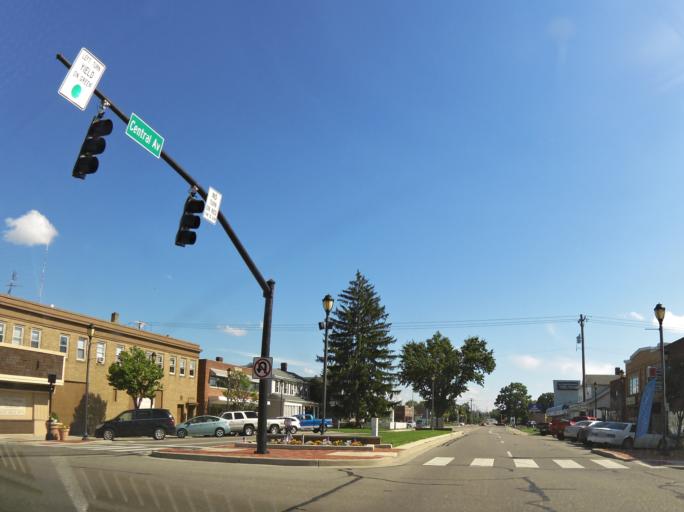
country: US
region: Ohio
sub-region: Greene County
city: Fairborn
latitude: 39.8216
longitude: -84.0212
